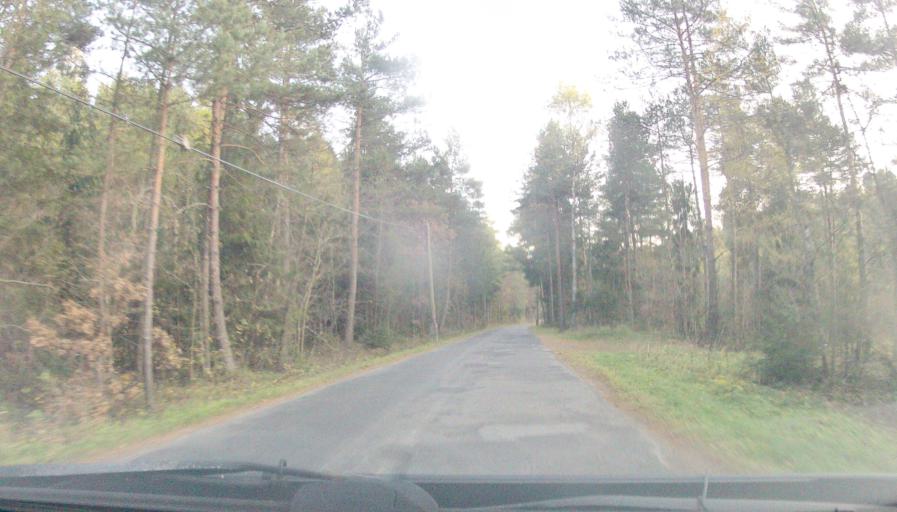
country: PL
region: Lesser Poland Voivodeship
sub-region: Powiat suski
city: Krzeszow
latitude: 49.7542
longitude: 19.4600
